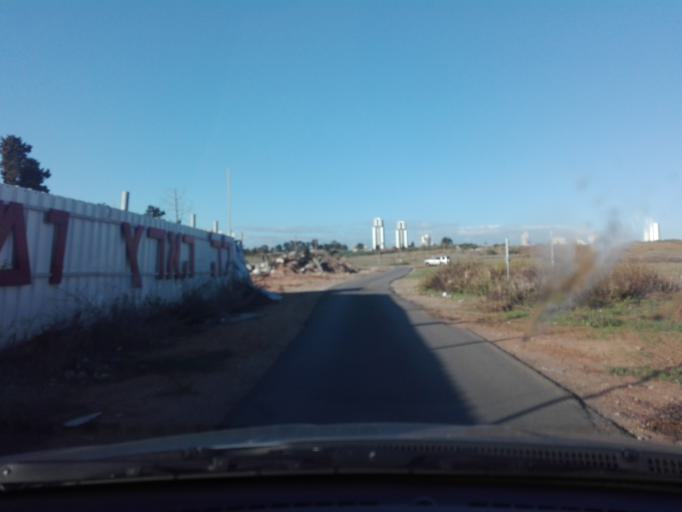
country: IL
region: Central District
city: Netanya
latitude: 32.3051
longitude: 34.8635
